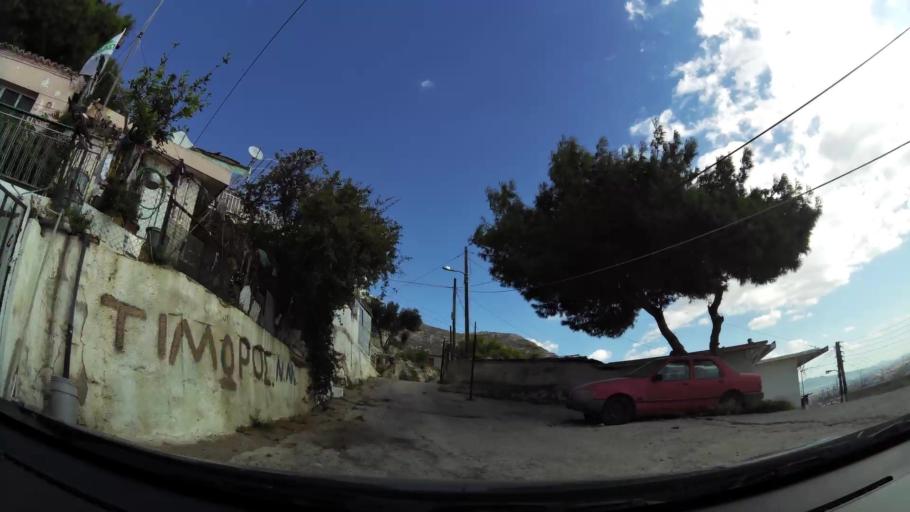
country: GR
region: Attica
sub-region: Nomos Piraios
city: Perama
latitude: 37.9678
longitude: 23.5814
